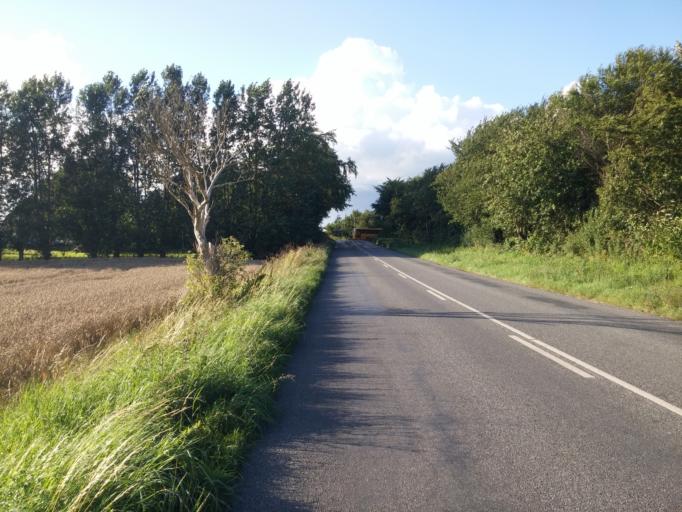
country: DK
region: Zealand
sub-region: Kalundborg Kommune
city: Svebolle
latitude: 55.7487
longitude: 11.3392
